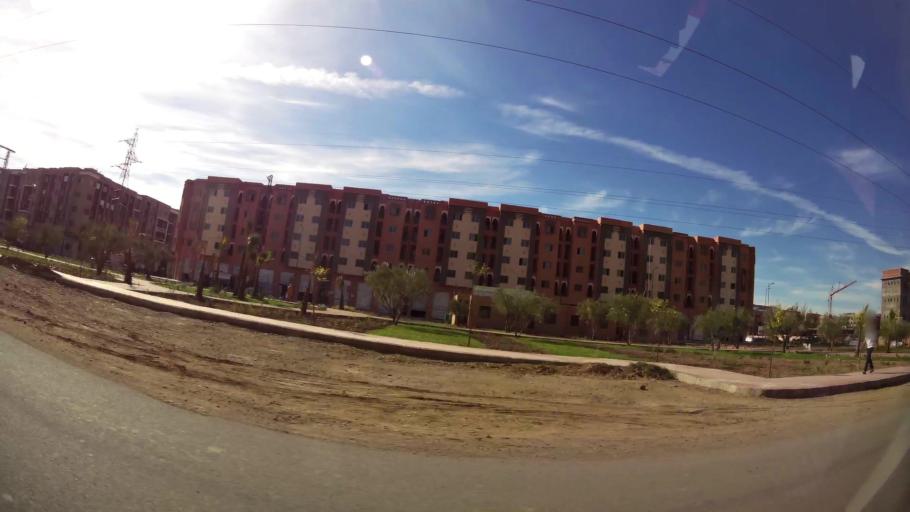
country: MA
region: Marrakech-Tensift-Al Haouz
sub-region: Marrakech
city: Marrakesh
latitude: 31.6487
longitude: -8.0360
